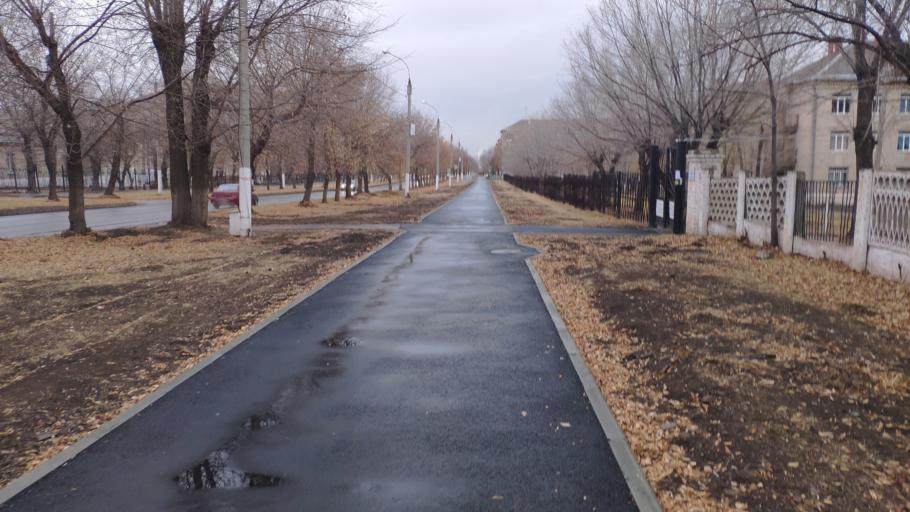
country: RU
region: Chelyabinsk
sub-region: Gorod Magnitogorsk
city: Magnitogorsk
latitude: 53.4044
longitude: 58.9684
